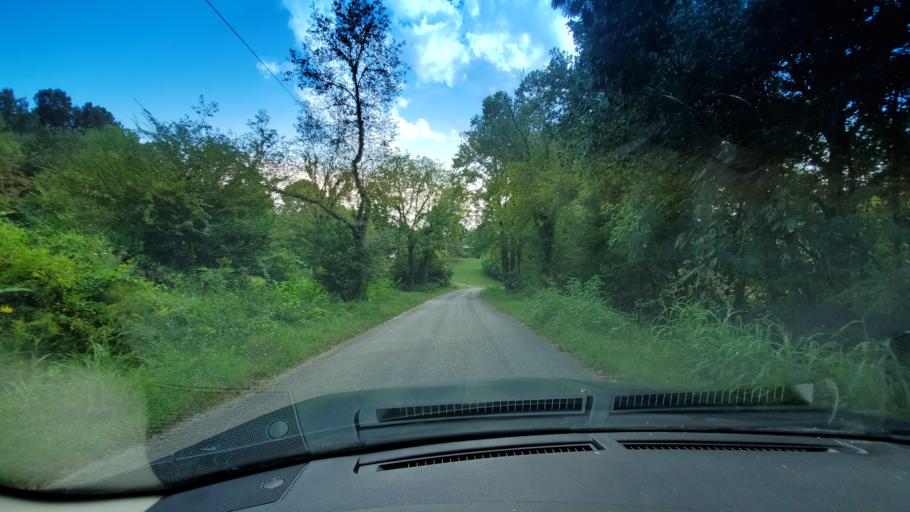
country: US
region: Tennessee
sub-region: Smith County
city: South Carthage
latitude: 36.2354
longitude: -85.9776
